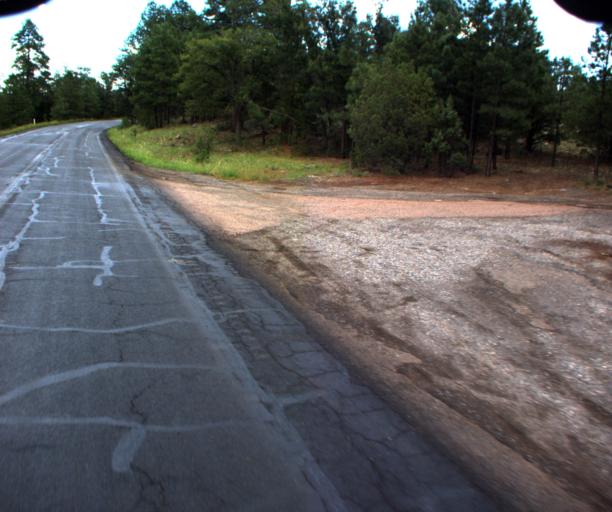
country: US
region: Arizona
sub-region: Gila County
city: Pine
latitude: 34.5133
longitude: -111.4855
